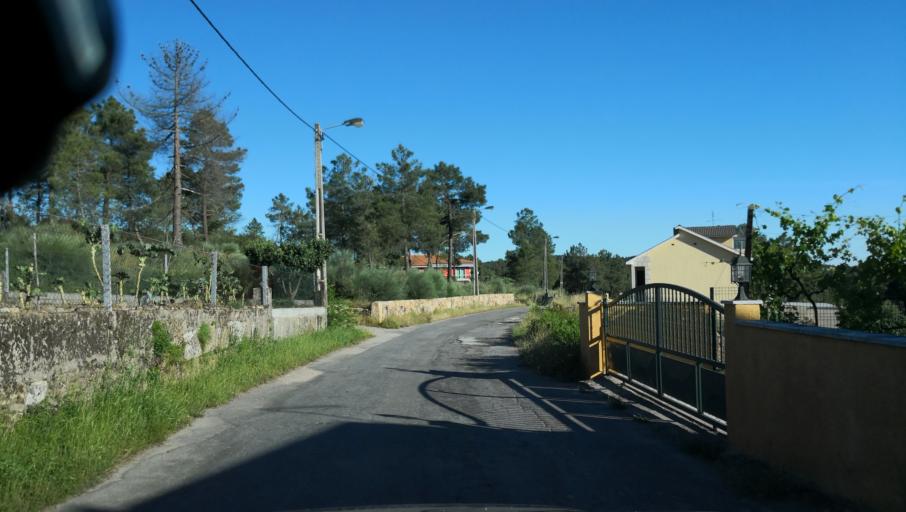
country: PT
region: Vila Real
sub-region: Vila Real
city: Vila Real
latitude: 41.3199
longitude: -7.6768
